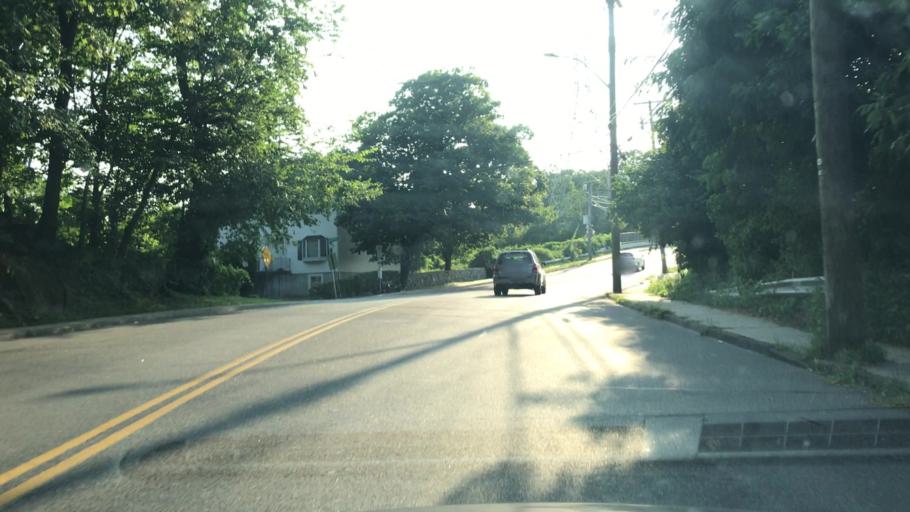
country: US
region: New York
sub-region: Westchester County
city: Bronxville
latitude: 40.9449
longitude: -73.8527
